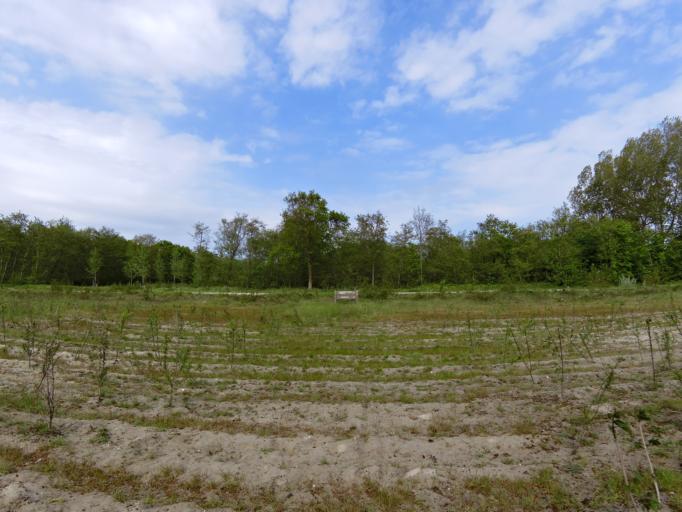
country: NL
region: South Holland
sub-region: Gemeente Goeree-Overflakkee
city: Ouddorp
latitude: 51.7834
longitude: 3.8917
